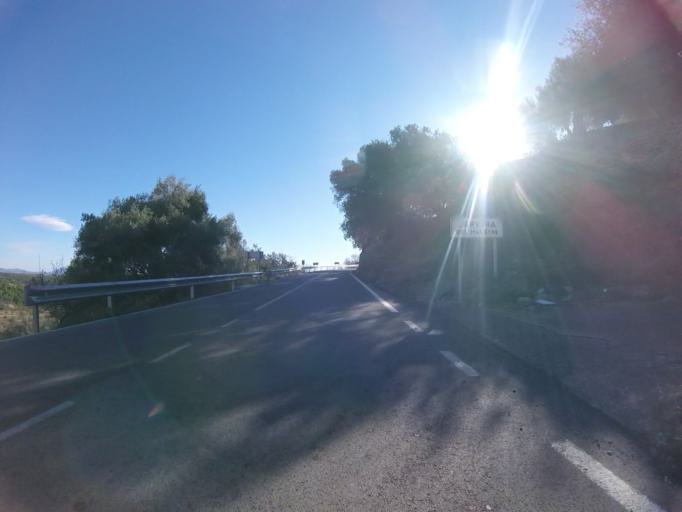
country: ES
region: Valencia
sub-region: Provincia de Castello
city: Cervera del Maestre
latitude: 40.4556
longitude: 0.2780
